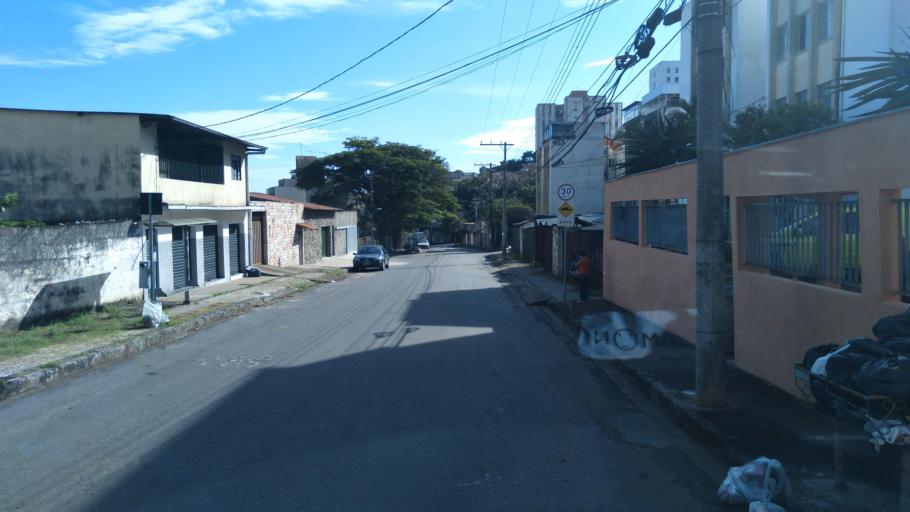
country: BR
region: Minas Gerais
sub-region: Contagem
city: Contagem
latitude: -19.9243
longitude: -44.0086
